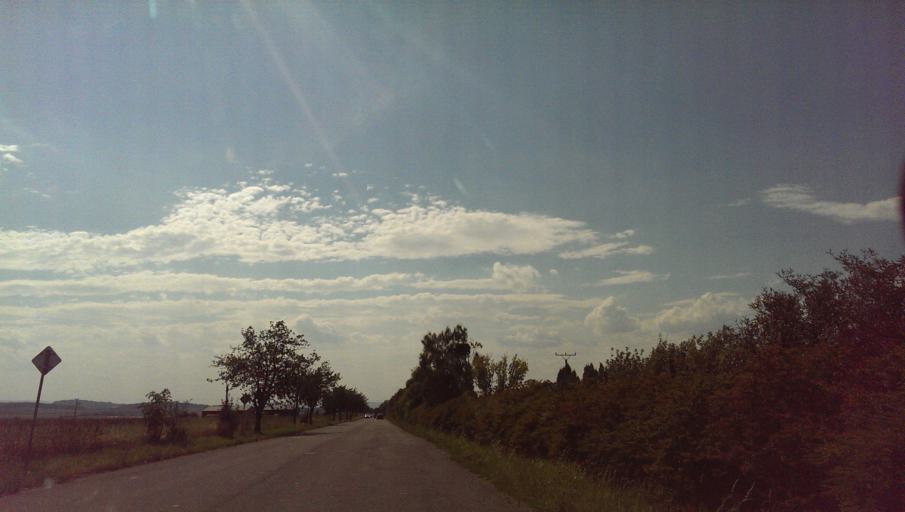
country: CZ
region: Zlin
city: Holesov
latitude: 49.3059
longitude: 17.6097
